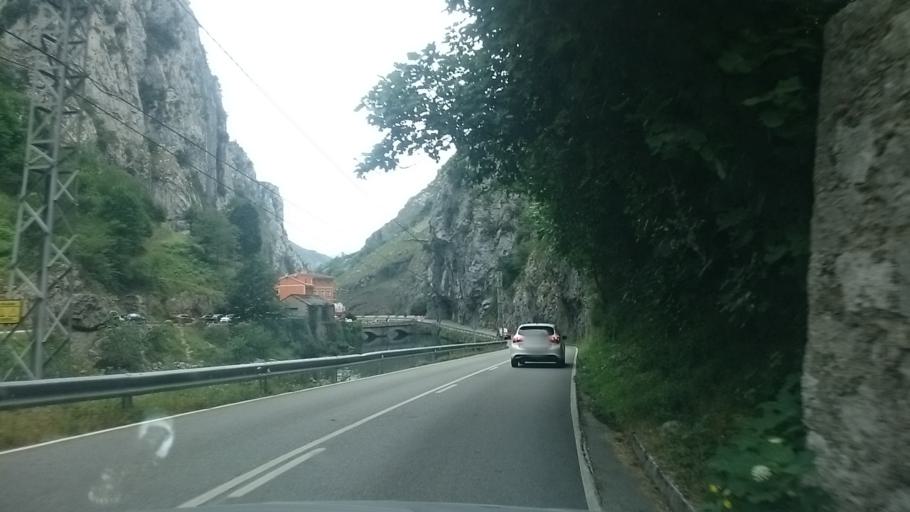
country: ES
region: Asturias
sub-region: Province of Asturias
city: Carrena
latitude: 43.2605
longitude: -4.8310
